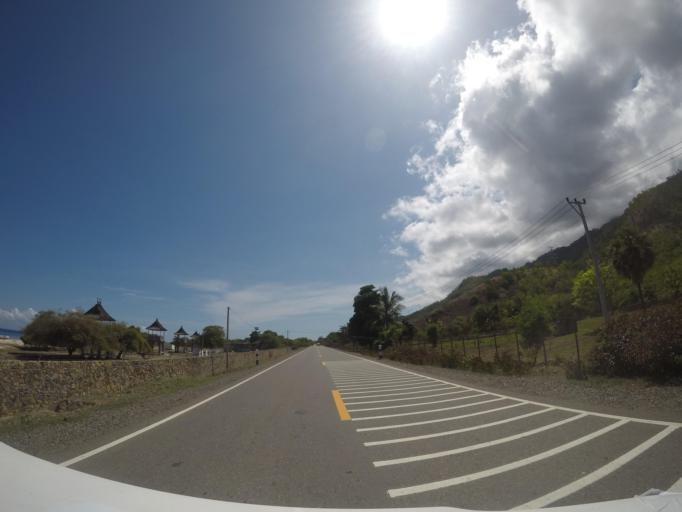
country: ID
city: Metinaro
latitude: -8.4785
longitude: 125.8472
